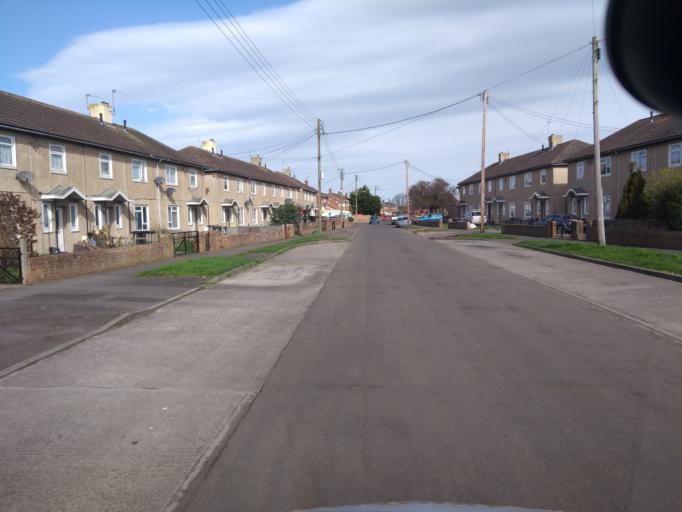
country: GB
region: England
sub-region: Somerset
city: Bridgwater
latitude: 51.1279
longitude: -2.9850
